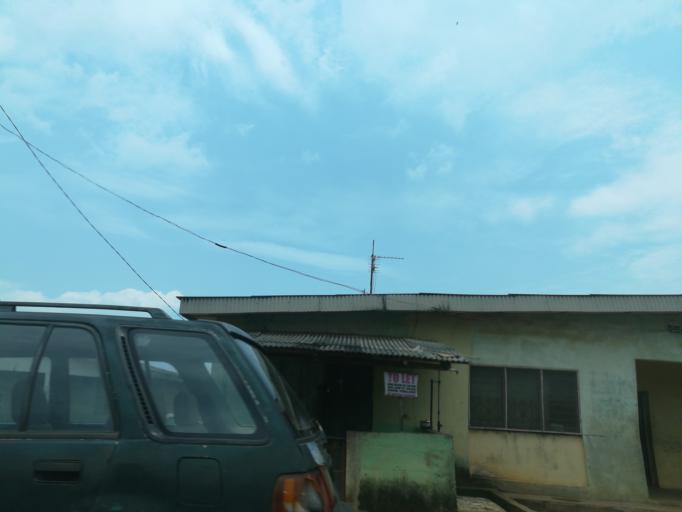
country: NG
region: Lagos
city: Ikorodu
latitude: 6.5637
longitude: 3.6005
